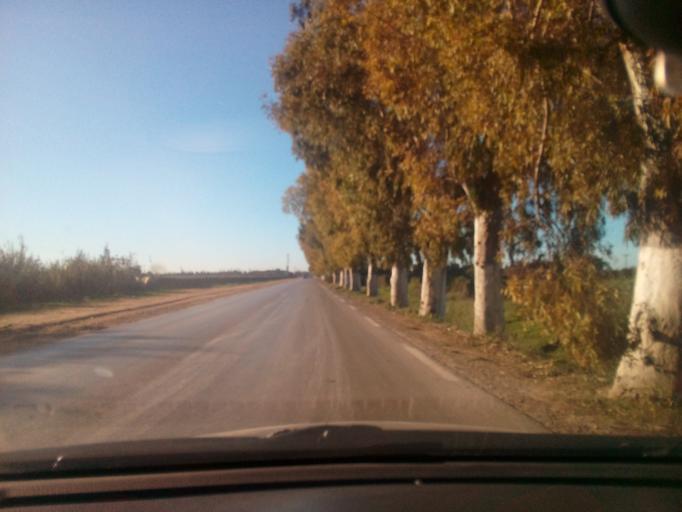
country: DZ
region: Mostaganem
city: Mostaganem
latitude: 35.8990
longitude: 0.2365
